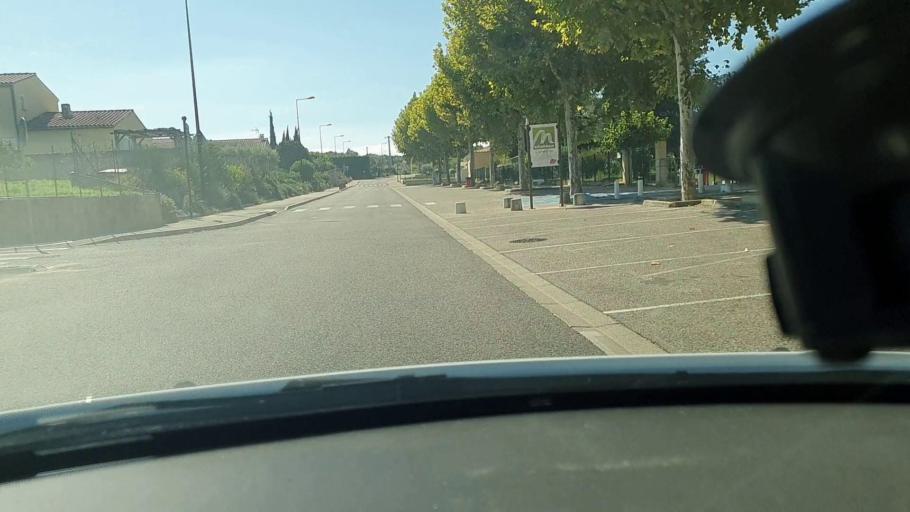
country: FR
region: Languedoc-Roussillon
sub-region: Departement du Gard
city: Saint-Paulet-de-Caisson
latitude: 44.2601
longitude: 4.5965
